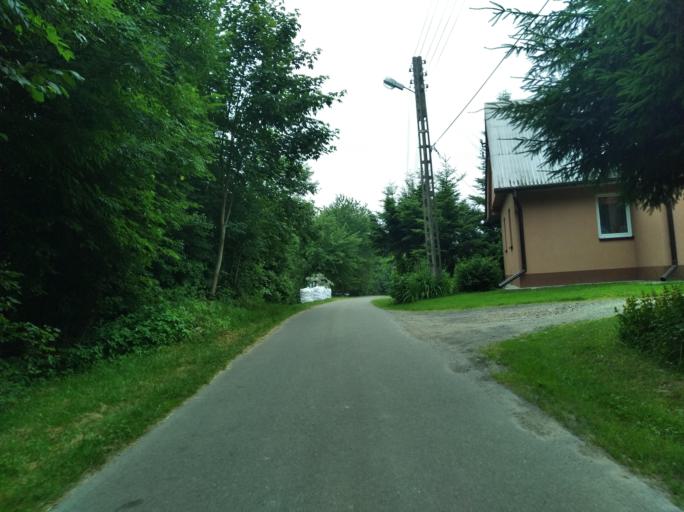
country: PL
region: Subcarpathian Voivodeship
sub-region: Powiat brzozowski
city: Jablonica Polska
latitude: 49.6903
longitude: 21.8863
